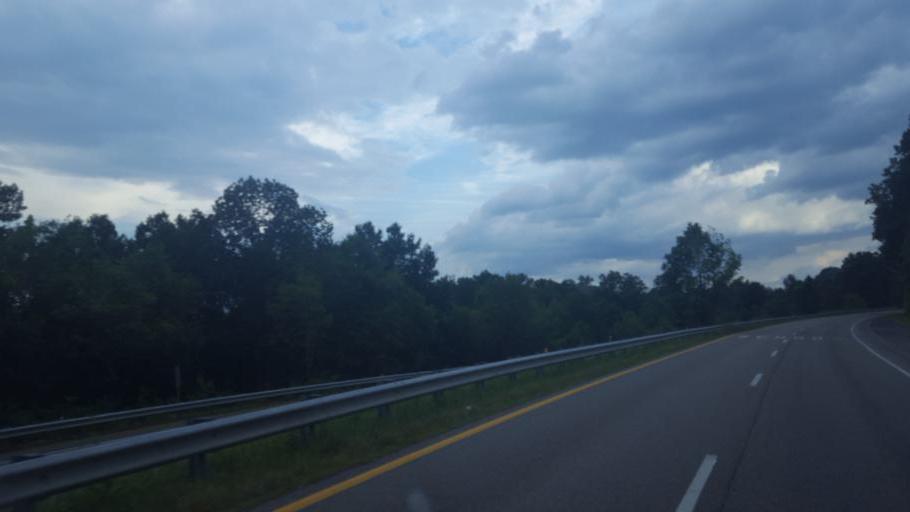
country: US
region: Virginia
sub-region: Wise County
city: Pound
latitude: 37.1126
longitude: -82.6053
